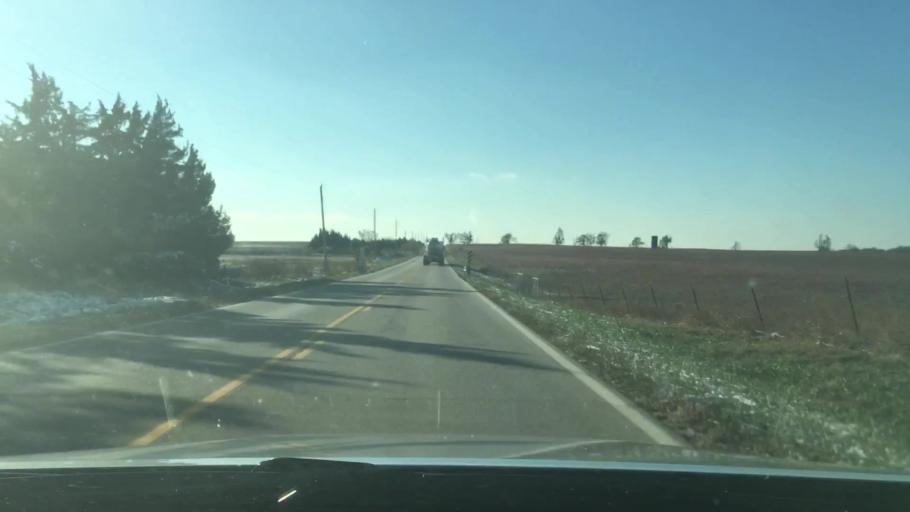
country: US
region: Kansas
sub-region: Reno County
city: Nickerson
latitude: 38.1449
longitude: -98.1433
